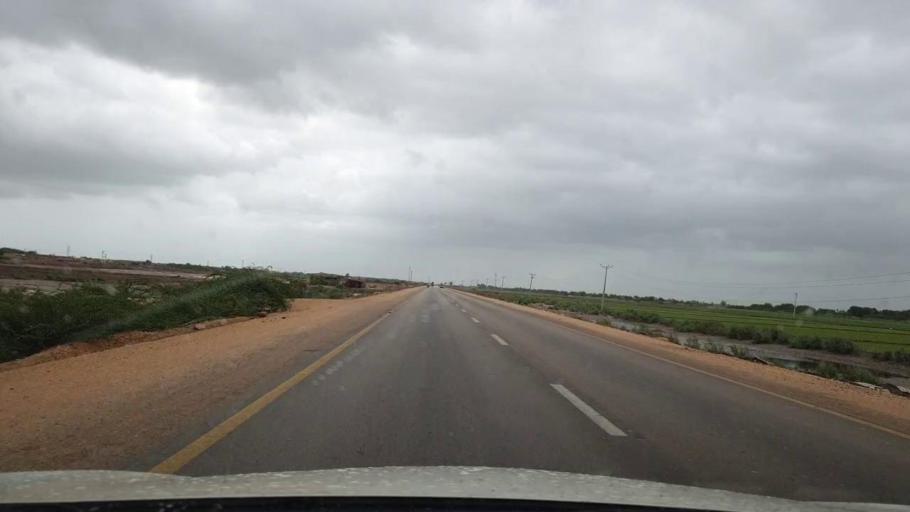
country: PK
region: Sindh
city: Badin
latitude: 24.6560
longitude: 68.7074
